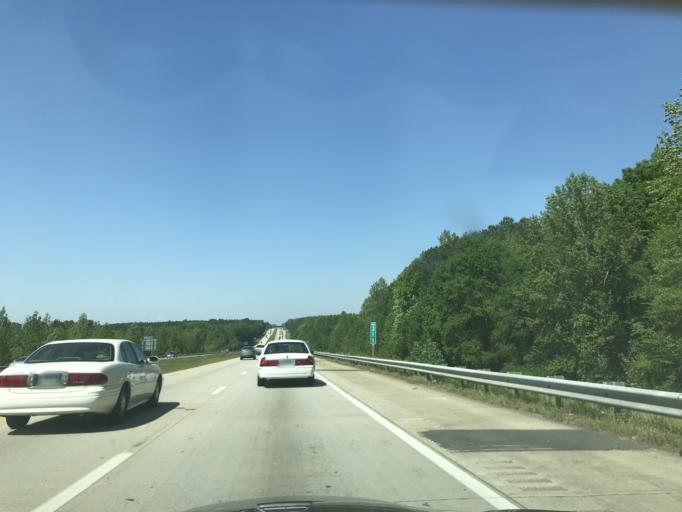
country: US
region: North Carolina
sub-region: Wake County
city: Garner
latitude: 35.6181
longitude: -78.5672
